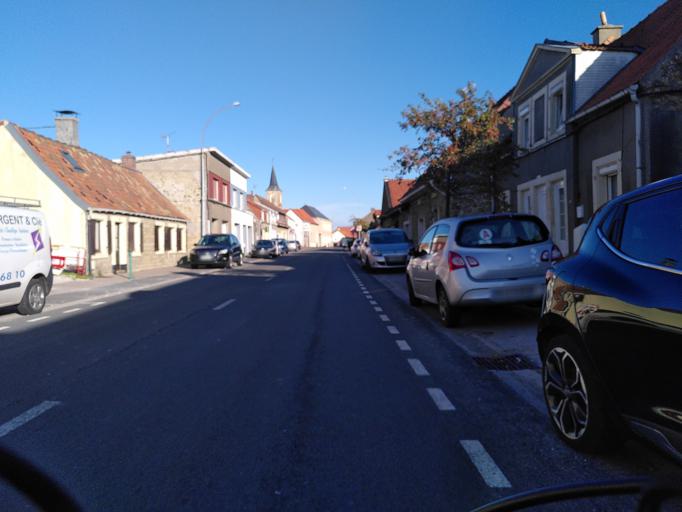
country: FR
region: Nord-Pas-de-Calais
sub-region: Departement du Pas-de-Calais
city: La Capelle-les-Boulogne
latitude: 50.7324
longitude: 1.7048
